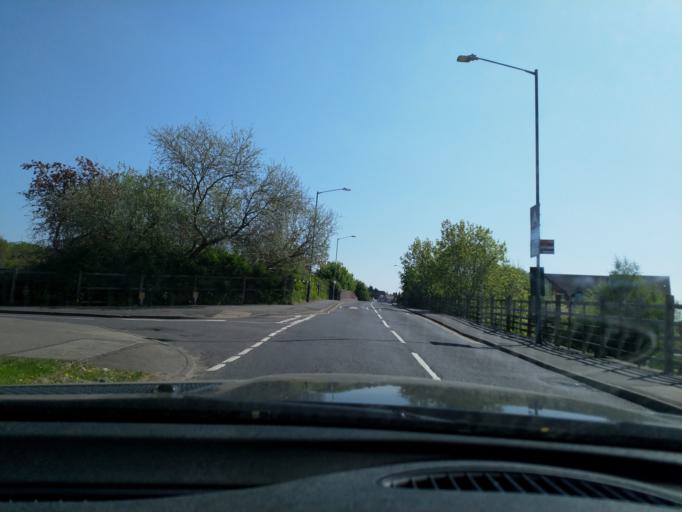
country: GB
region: England
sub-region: Warwickshire
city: Warwick
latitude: 52.2875
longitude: -1.5916
